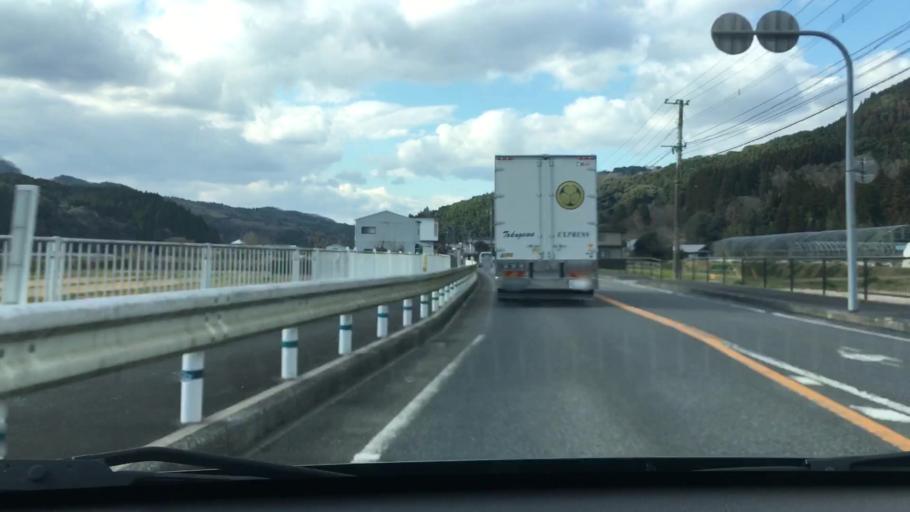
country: JP
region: Oita
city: Usuki
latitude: 33.0055
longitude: 131.7248
